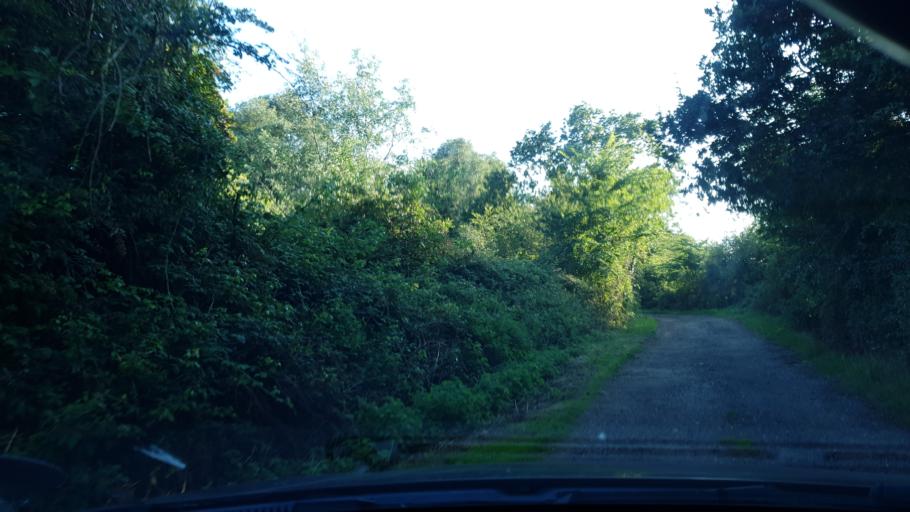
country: GB
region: England
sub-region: Essex
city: Frinton-on-Sea
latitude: 51.8481
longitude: 1.2420
